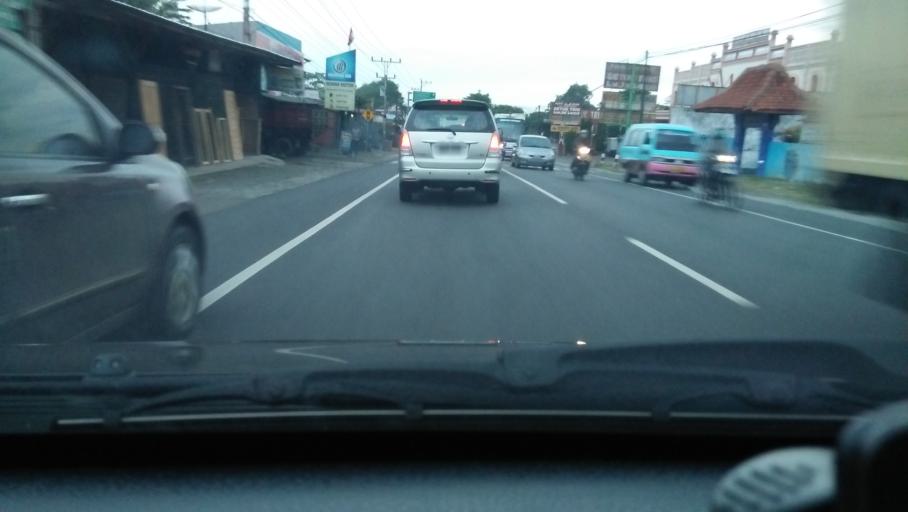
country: ID
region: Central Java
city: Magelang
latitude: -7.4218
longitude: 110.2323
